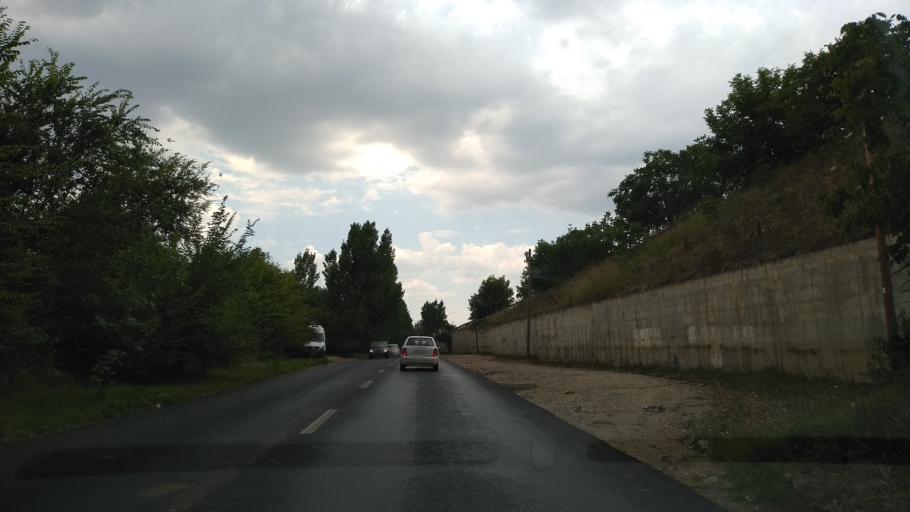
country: RO
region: Ilfov
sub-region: Comuna Popesti-Leordeni
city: Popesti-Leordeni
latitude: 44.3909
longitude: 26.1513
